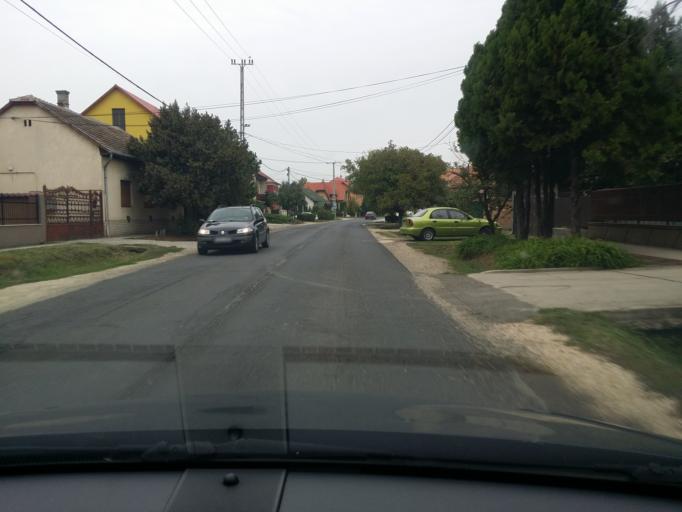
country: HU
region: Pest
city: Alsonemedi
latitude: 47.3209
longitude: 19.1514
